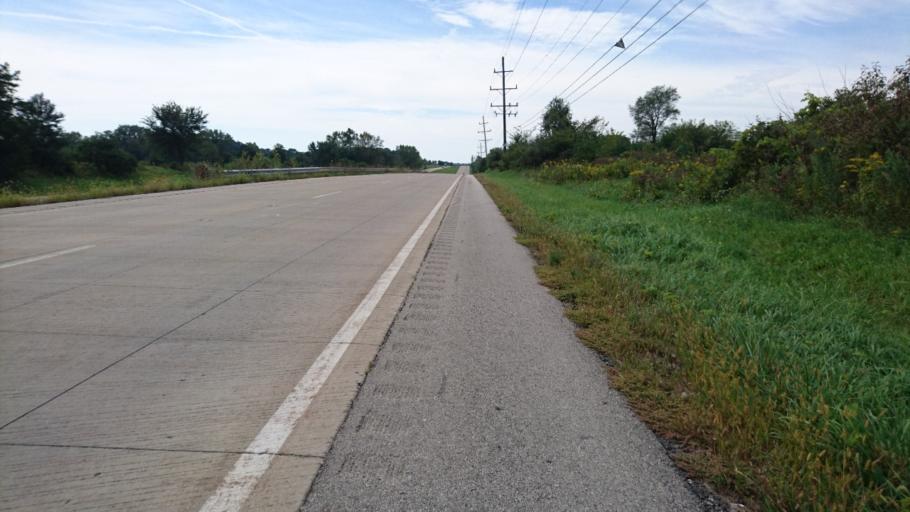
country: US
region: Illinois
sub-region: Will County
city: Elwood
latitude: 41.3872
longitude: -88.1210
